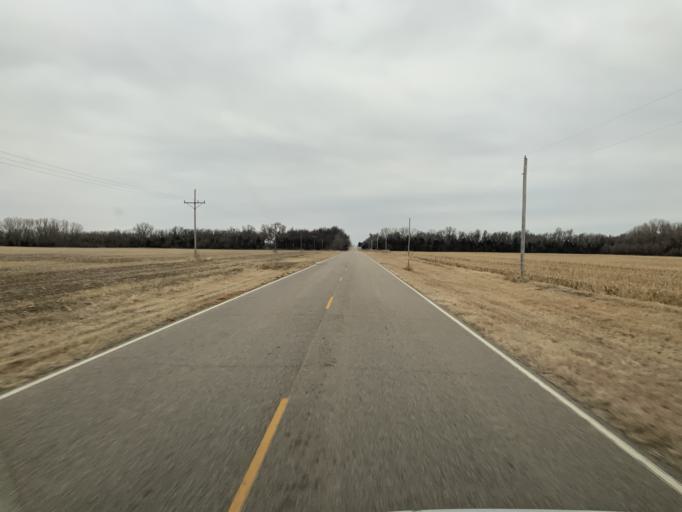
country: US
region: Kansas
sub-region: Reno County
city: South Hutchinson
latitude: 37.9383
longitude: -98.0869
